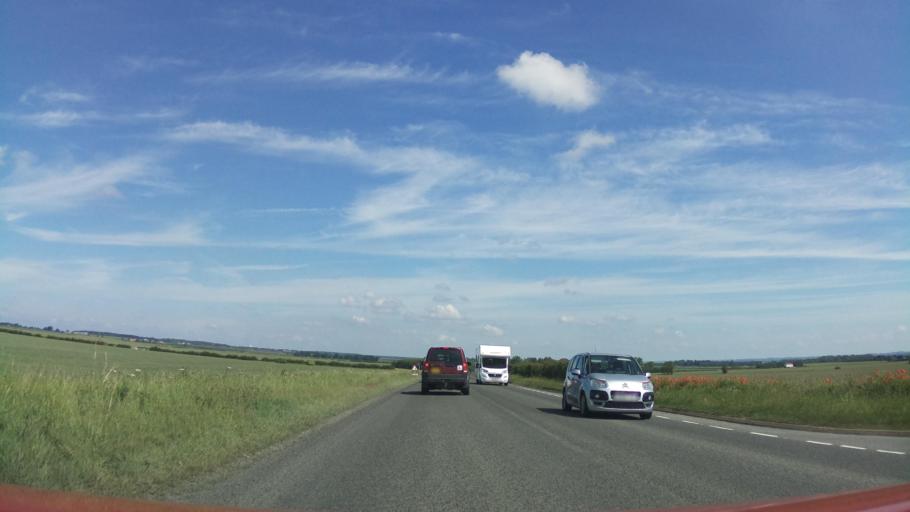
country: GB
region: England
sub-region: North Lincolnshire
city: Redbourne
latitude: 53.4563
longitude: -0.5518
